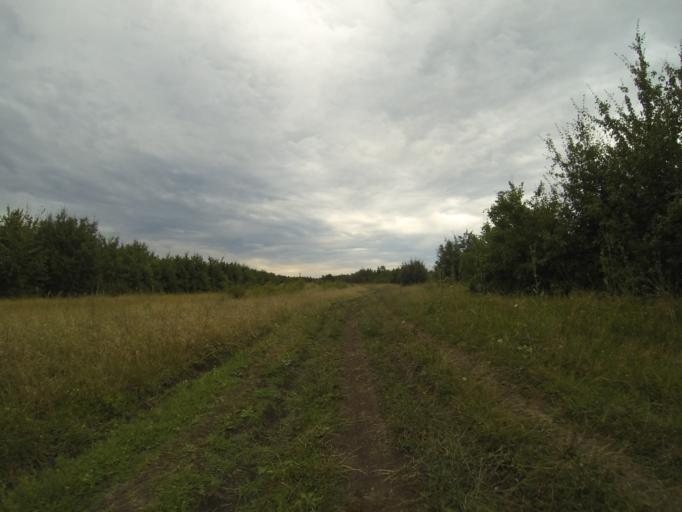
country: RO
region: Dolj
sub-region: Comuna Filiasi
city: Fratostita
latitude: 44.5794
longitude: 23.6086
